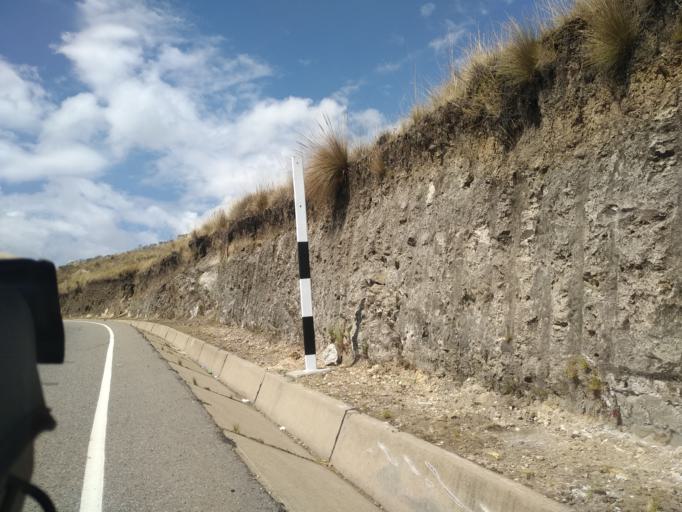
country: PE
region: La Libertad
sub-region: Provincia de Santiago de Chuco
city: Quiruvilca
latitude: -7.9194
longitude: -78.1526
